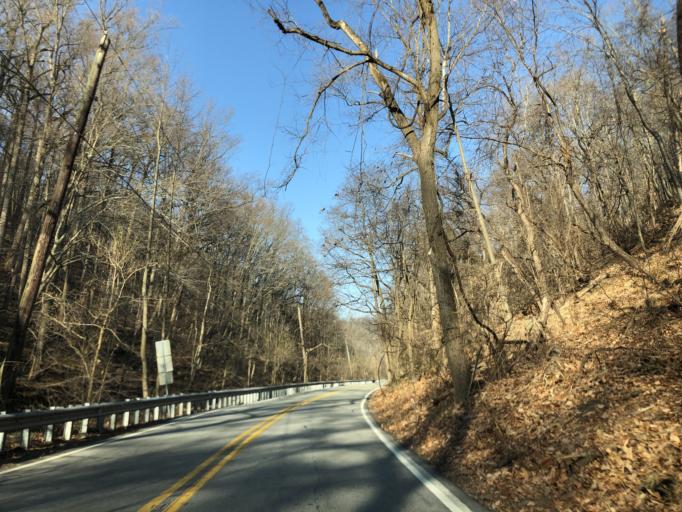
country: US
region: Pennsylvania
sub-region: Chester County
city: Chesterbrook
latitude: 40.0882
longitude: -75.4563
